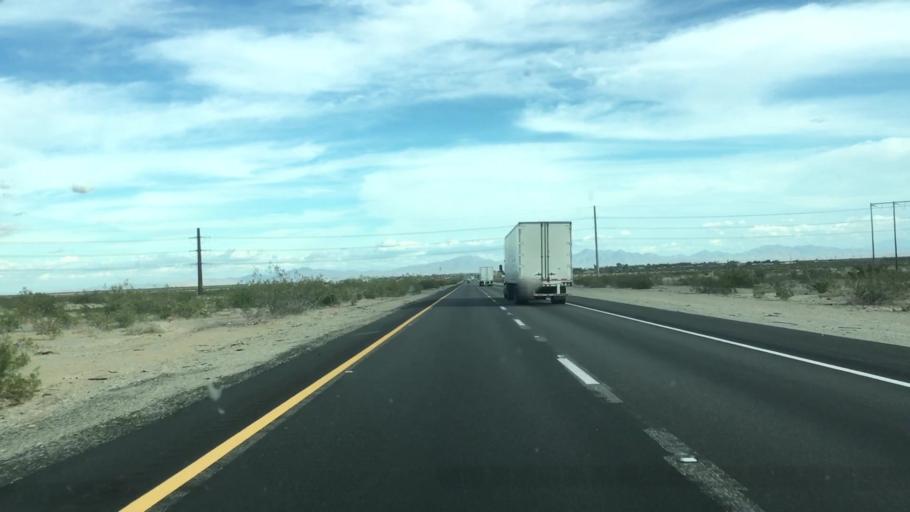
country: US
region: California
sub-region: Riverside County
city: Mesa Verde
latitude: 33.6088
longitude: -114.7571
